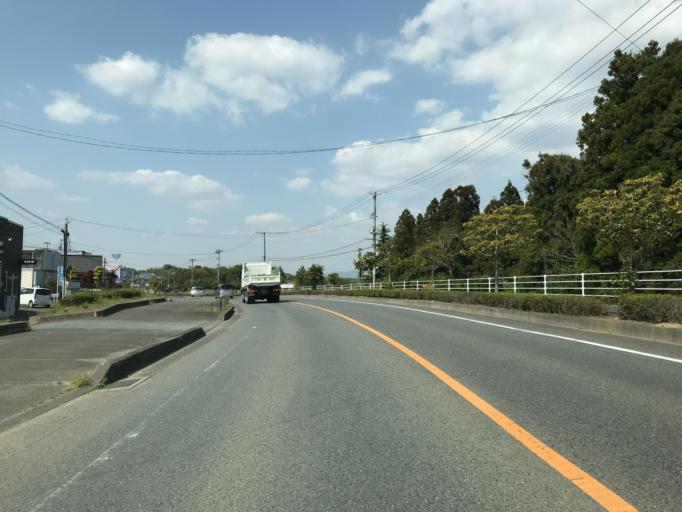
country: JP
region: Ibaraki
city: Kitaibaraki
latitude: 36.8938
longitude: 140.7679
